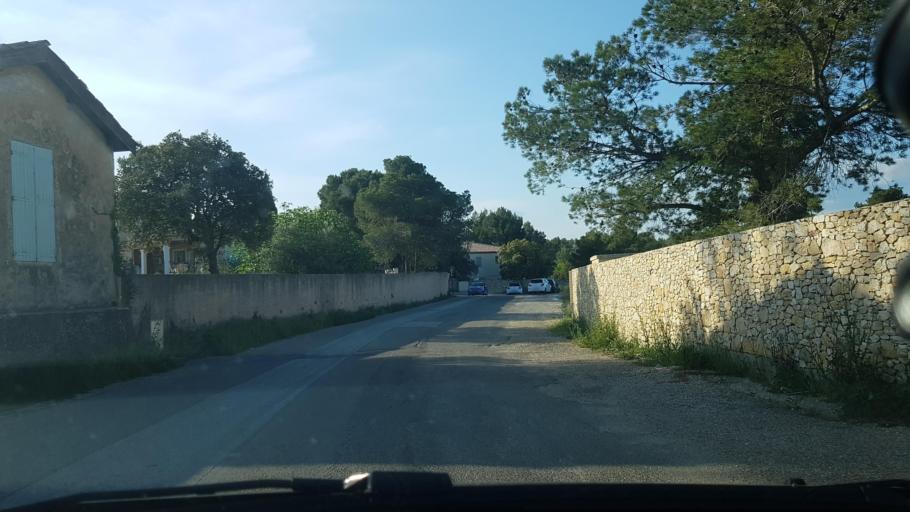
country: FR
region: Languedoc-Roussillon
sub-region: Departement du Gard
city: Caveirac
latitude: 43.8447
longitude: 4.2956
